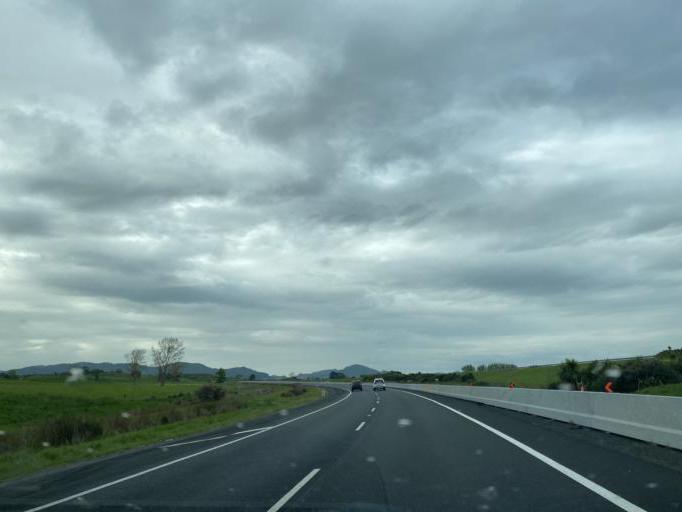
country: NZ
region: Waikato
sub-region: Waikato District
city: Ngaruawahia
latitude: -37.6847
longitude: 175.2152
